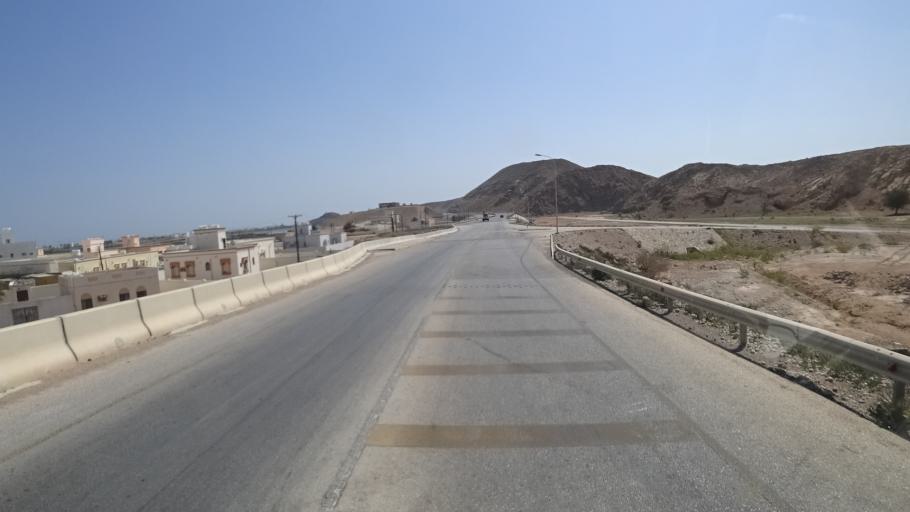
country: OM
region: Ash Sharqiyah
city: Sur
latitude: 22.5480
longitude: 59.5231
